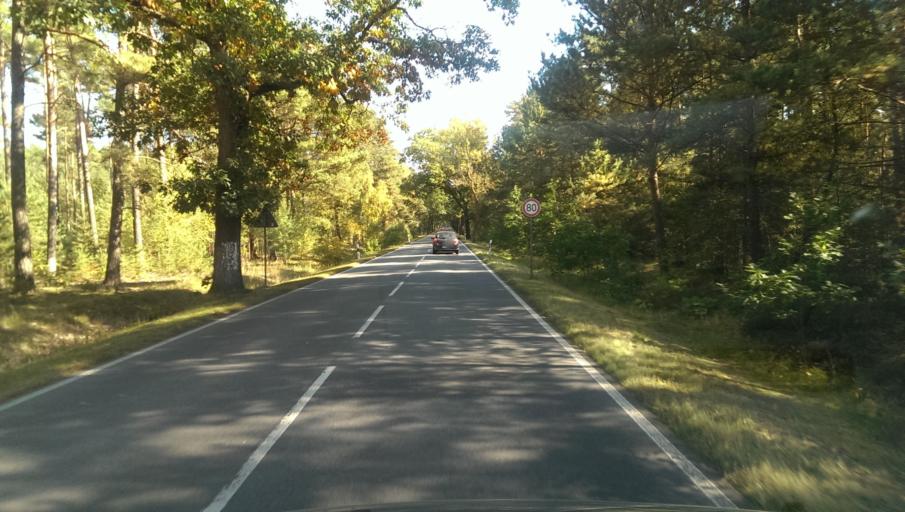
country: DE
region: Brandenburg
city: Halbe
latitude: 52.1138
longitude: 13.6624
